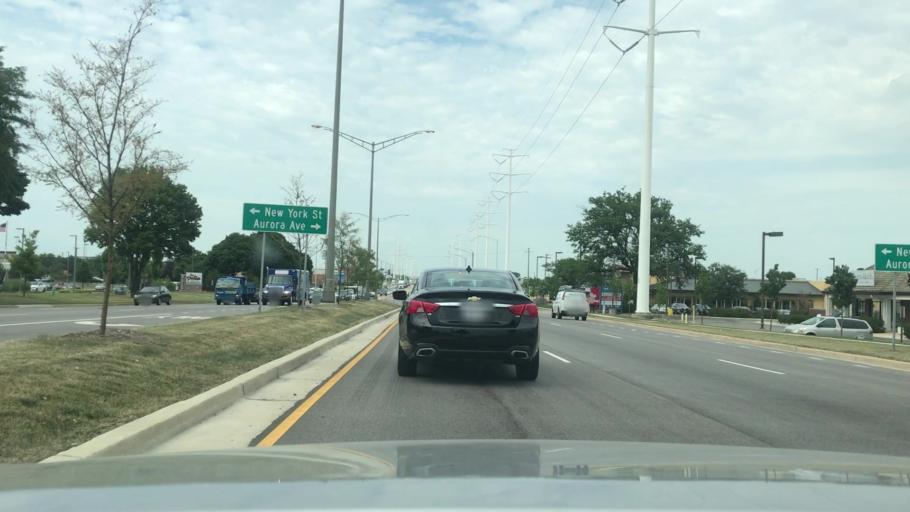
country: US
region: Illinois
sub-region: DuPage County
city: Naperville
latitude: 41.7601
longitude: -88.2059
